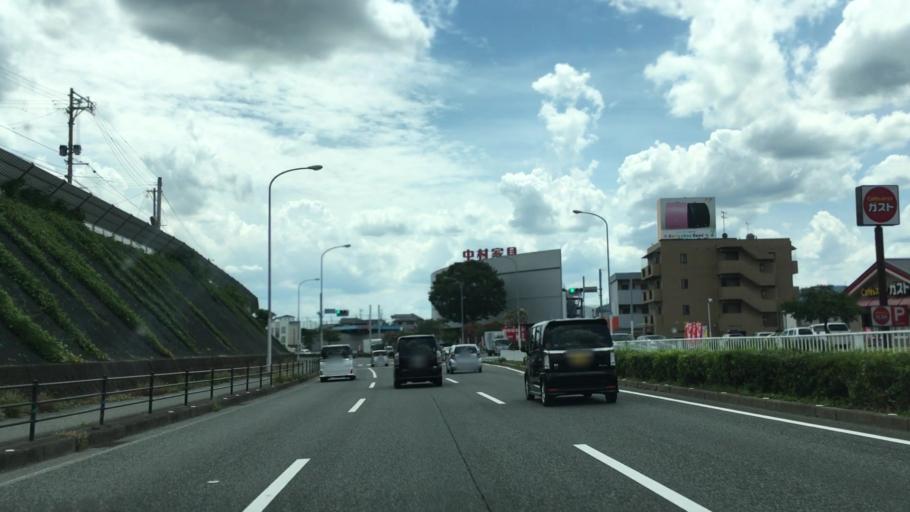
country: JP
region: Fukuoka
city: Dazaifu
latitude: 33.5007
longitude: 130.5314
